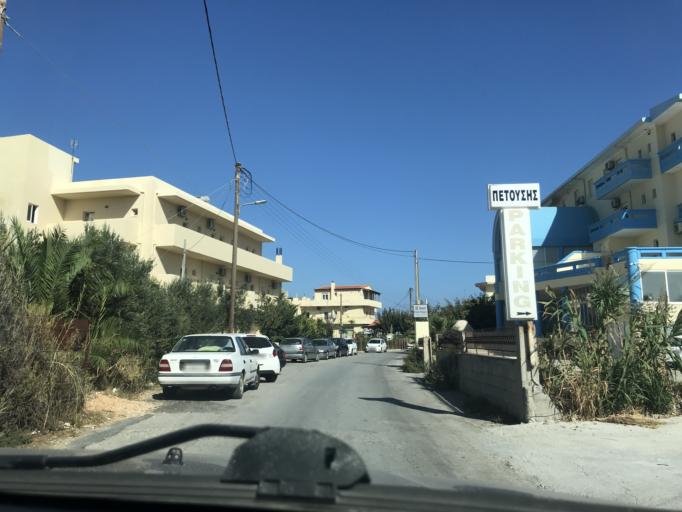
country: GR
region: Crete
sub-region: Nomos Irakleiou
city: Gazi
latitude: 35.3364
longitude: 25.0678
